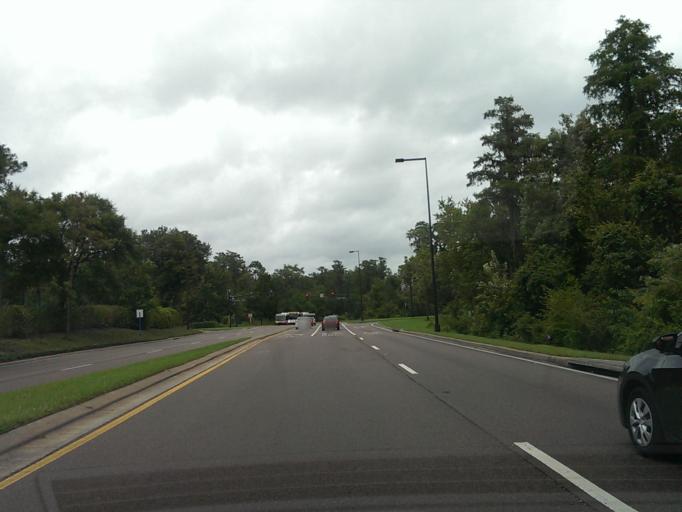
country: US
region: Florida
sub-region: Osceola County
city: Celebration
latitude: 28.3717
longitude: -81.5412
